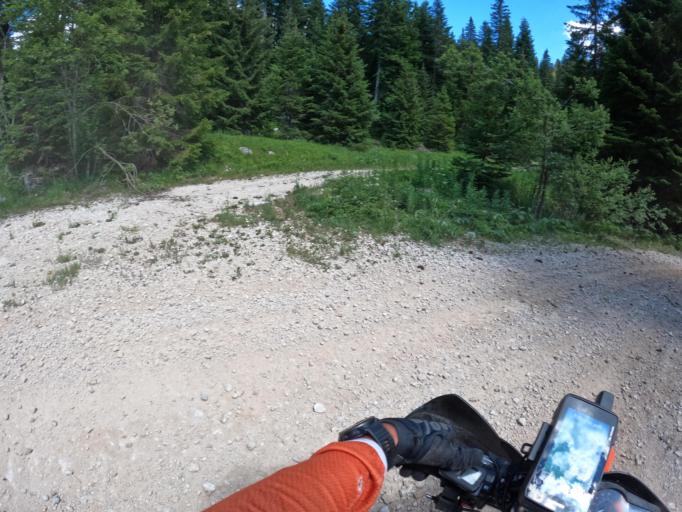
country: BA
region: Federation of Bosnia and Herzegovina
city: Livno
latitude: 43.9162
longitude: 17.1056
